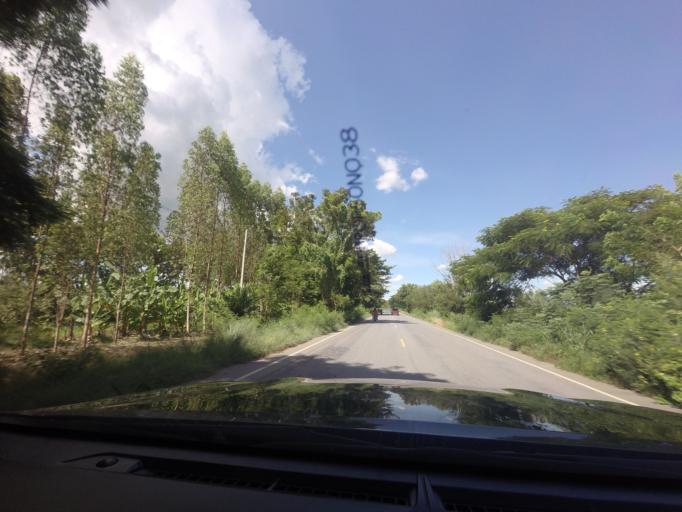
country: TH
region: Kanchanaburi
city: Phanom Thuan
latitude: 14.1753
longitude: 99.7826
